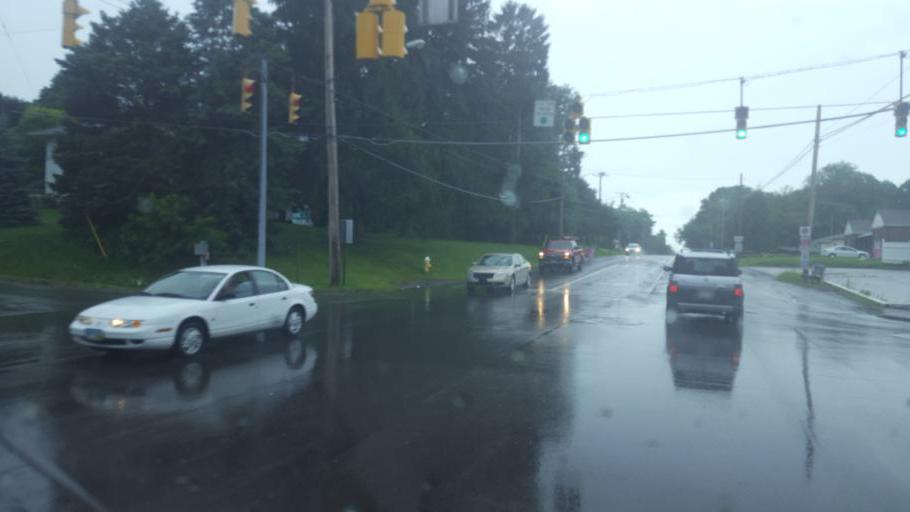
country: US
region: Ohio
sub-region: Richland County
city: Ontario
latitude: 40.7596
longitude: -82.5709
